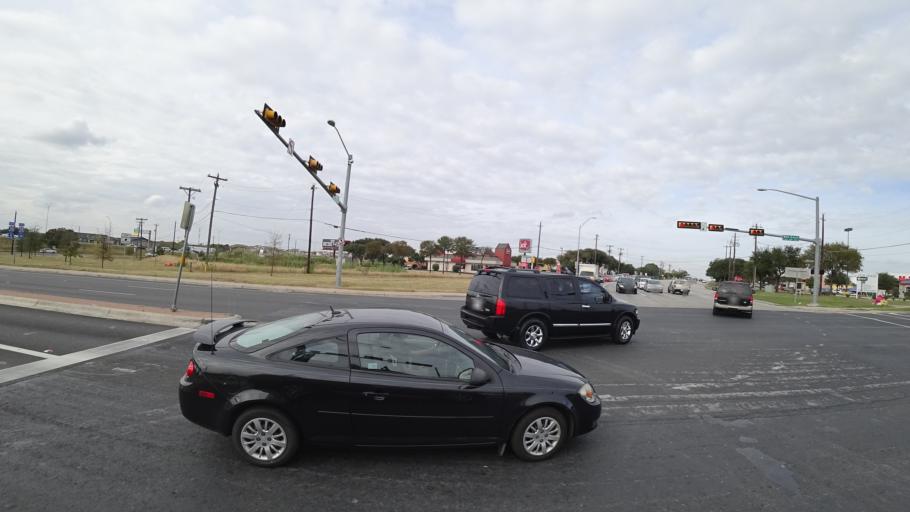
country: US
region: Texas
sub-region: Travis County
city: Wells Branch
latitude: 30.4411
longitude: -97.6664
